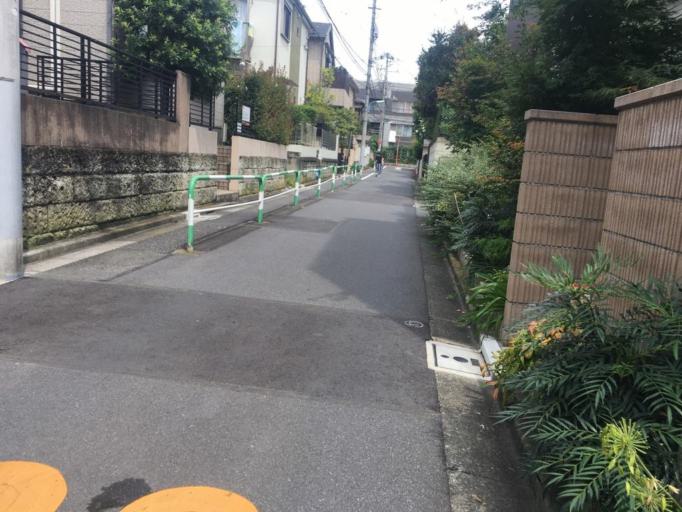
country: JP
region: Tokyo
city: Tokyo
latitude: 35.7191
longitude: 139.7009
